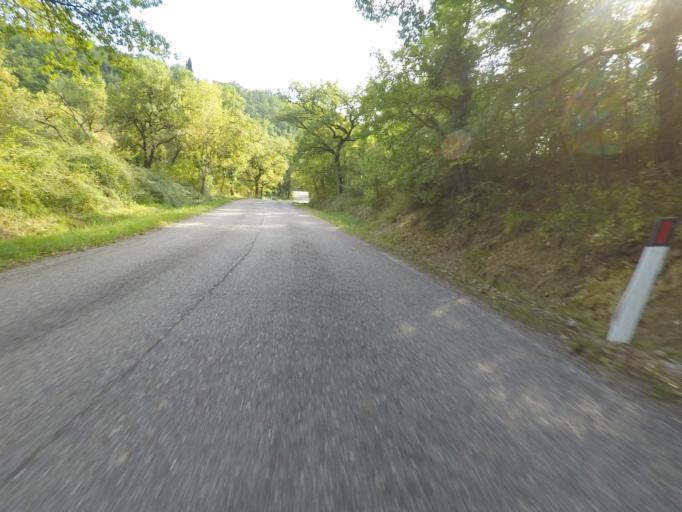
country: IT
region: Tuscany
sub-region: Provincia di Siena
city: Radda in Chianti
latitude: 43.5114
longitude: 11.4058
